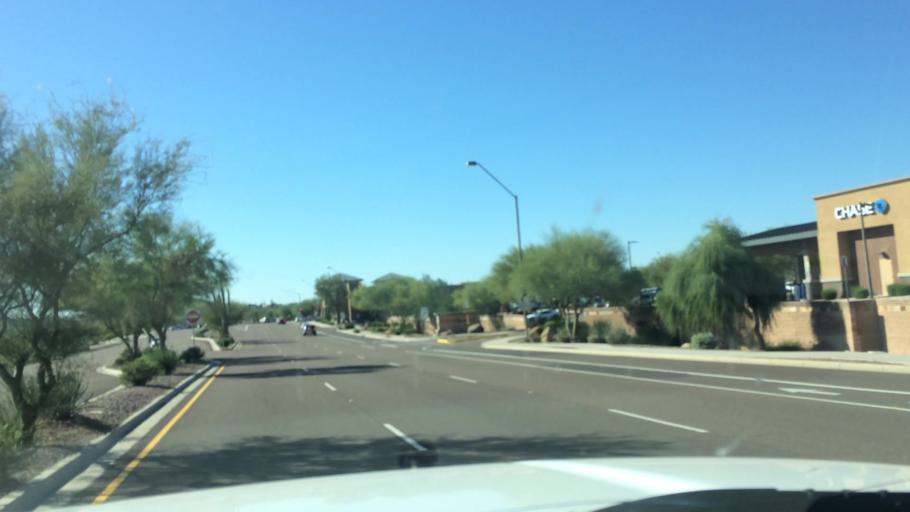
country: US
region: Arizona
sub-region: Maricopa County
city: Anthem
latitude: 33.8432
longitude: -112.1323
